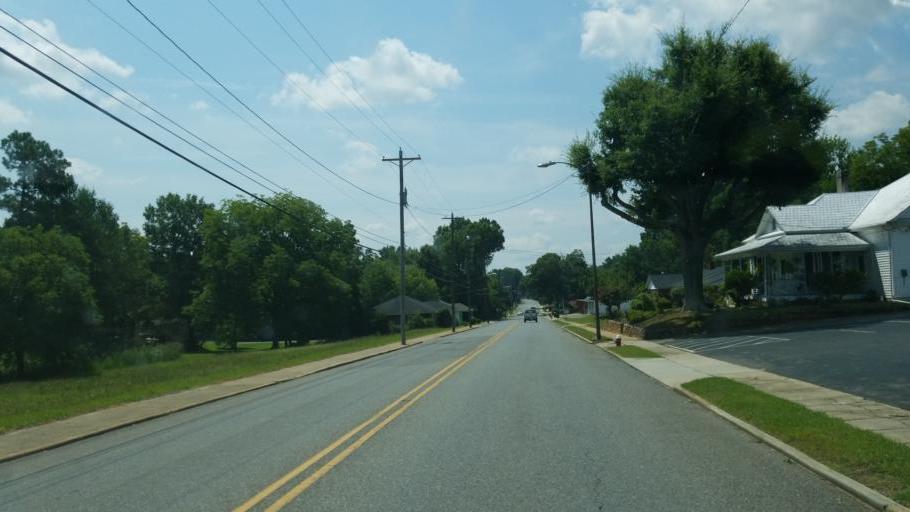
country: US
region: North Carolina
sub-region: Gaston County
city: Cherryville
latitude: 35.3769
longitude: -81.3789
